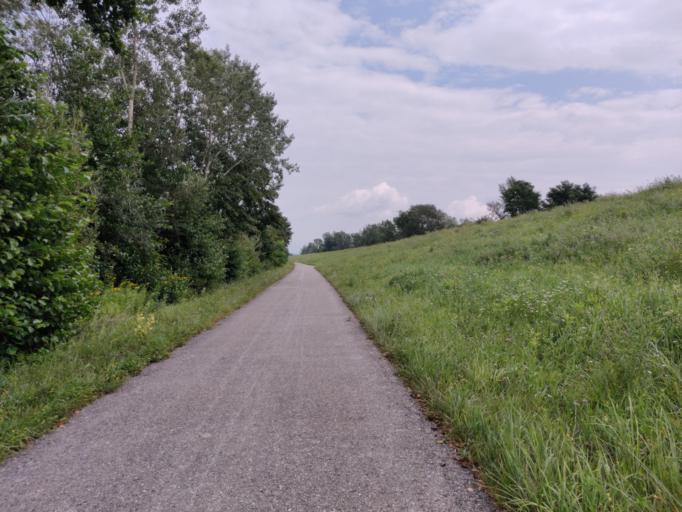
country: AT
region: Lower Austria
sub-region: Politischer Bezirk Melk
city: Marbach an der Donau
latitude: 48.2121
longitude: 15.1647
